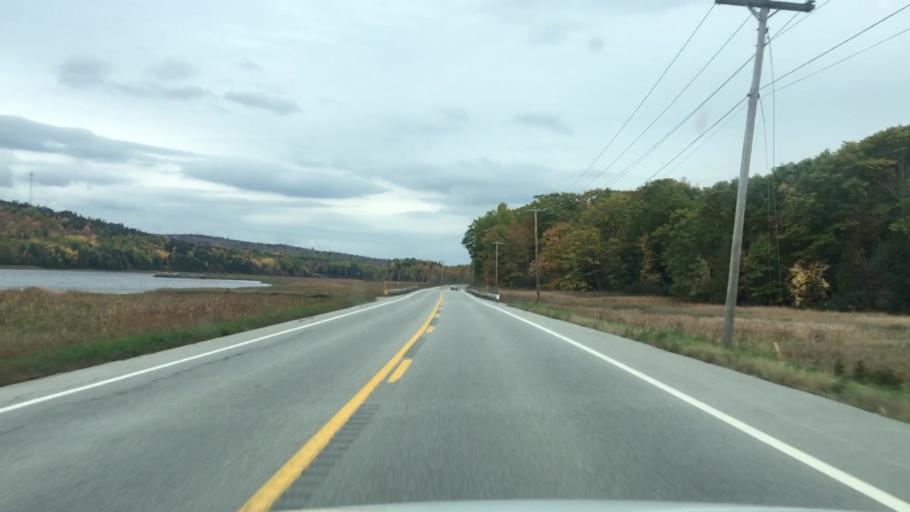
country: US
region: Maine
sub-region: Waldo County
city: Frankfort
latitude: 44.5887
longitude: -68.8653
